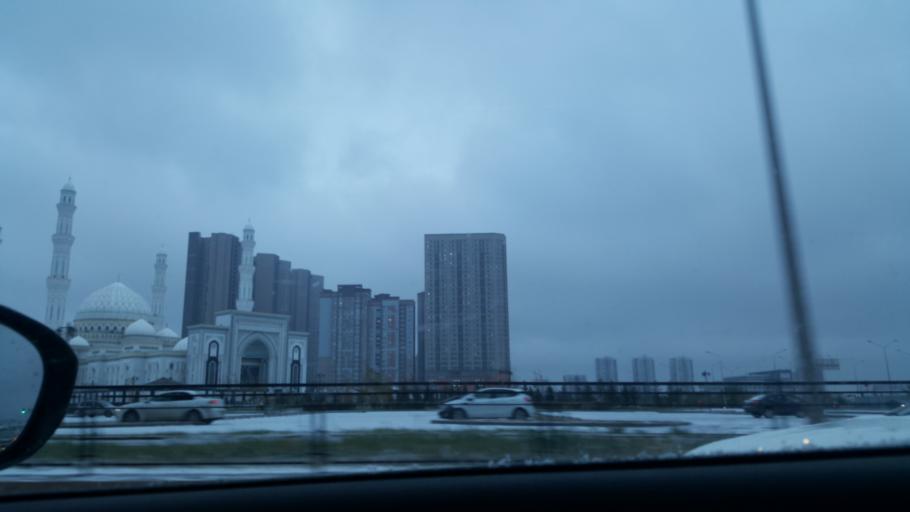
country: KZ
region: Astana Qalasy
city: Astana
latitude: 51.1261
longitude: 71.4761
